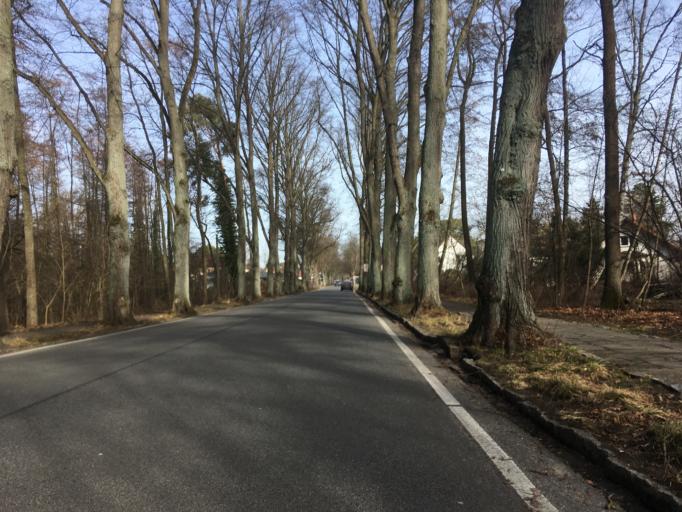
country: DE
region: Berlin
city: Schmockwitz
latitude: 52.3918
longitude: 13.6279
